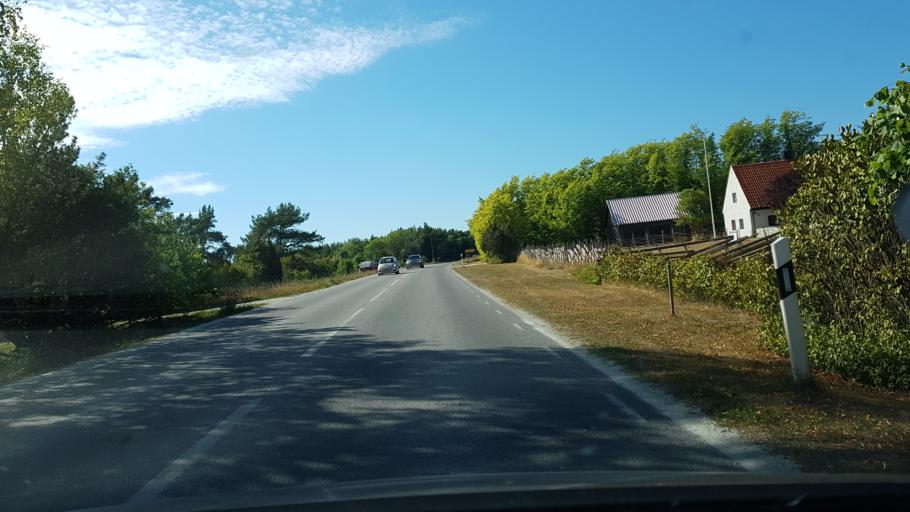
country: SE
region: Gotland
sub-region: Gotland
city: Klintehamn
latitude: 57.4086
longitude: 18.1660
